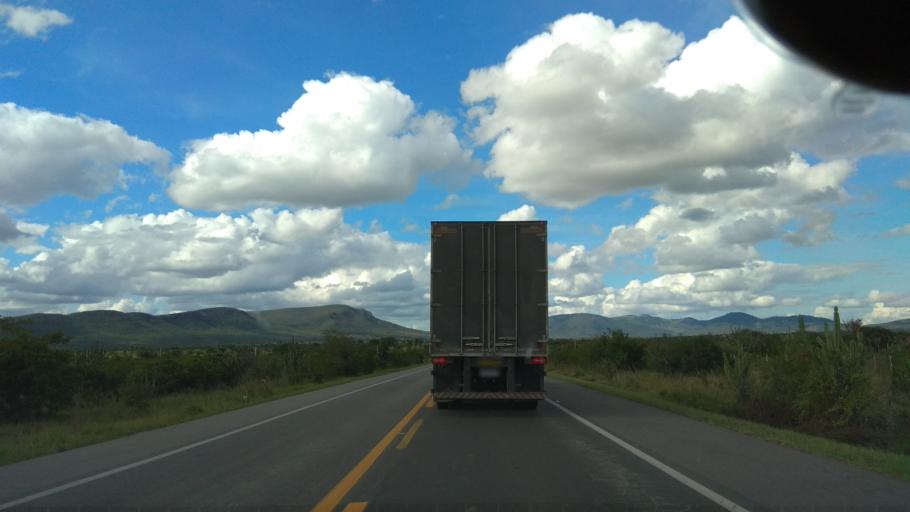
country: BR
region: Bahia
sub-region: Castro Alves
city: Castro Alves
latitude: -12.6775
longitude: -39.6645
